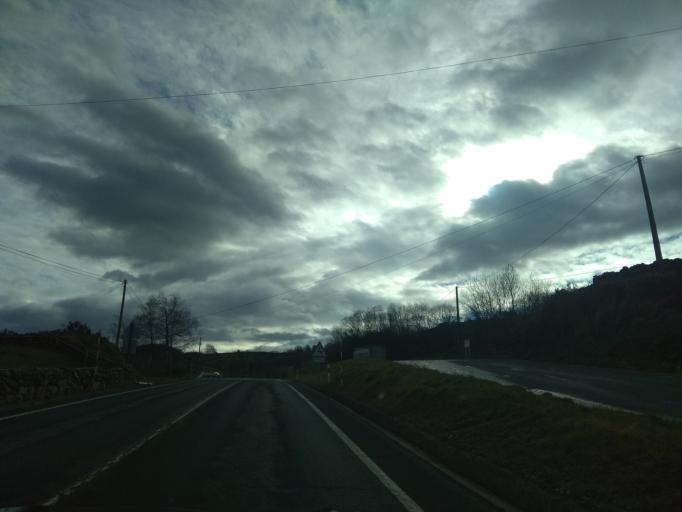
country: ES
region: Cantabria
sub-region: Provincia de Cantabria
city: San Pedro del Romeral
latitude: 43.0765
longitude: -3.8897
